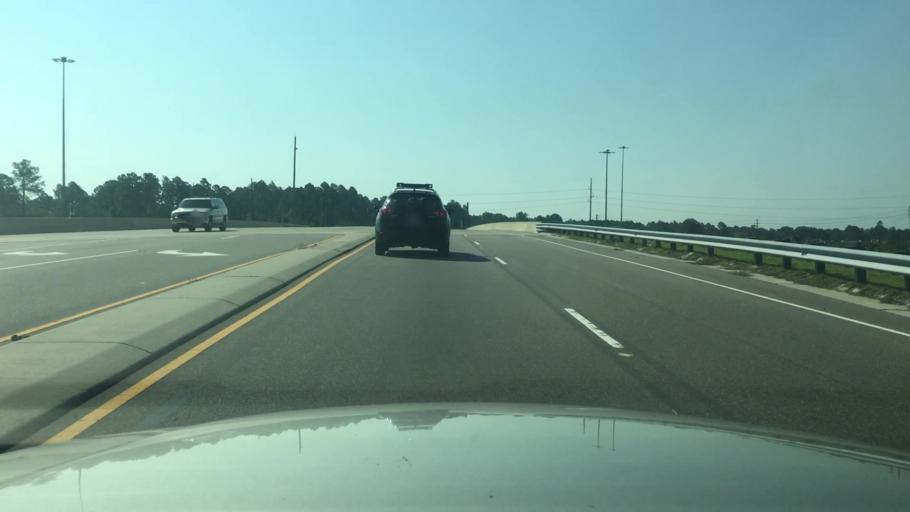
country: US
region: North Carolina
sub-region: Cumberland County
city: Spring Lake
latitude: 35.1405
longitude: -78.9072
